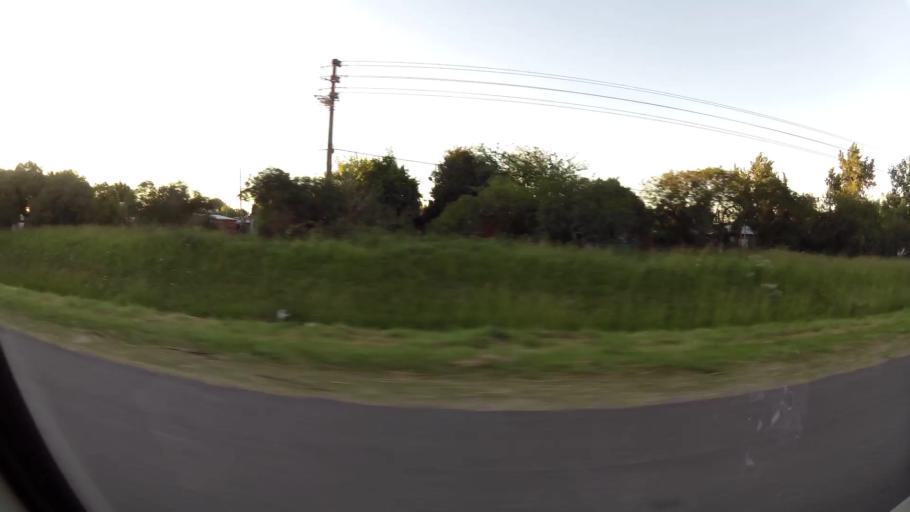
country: AR
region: Buenos Aires
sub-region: Partido de Quilmes
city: Quilmes
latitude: -34.8110
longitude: -58.1765
